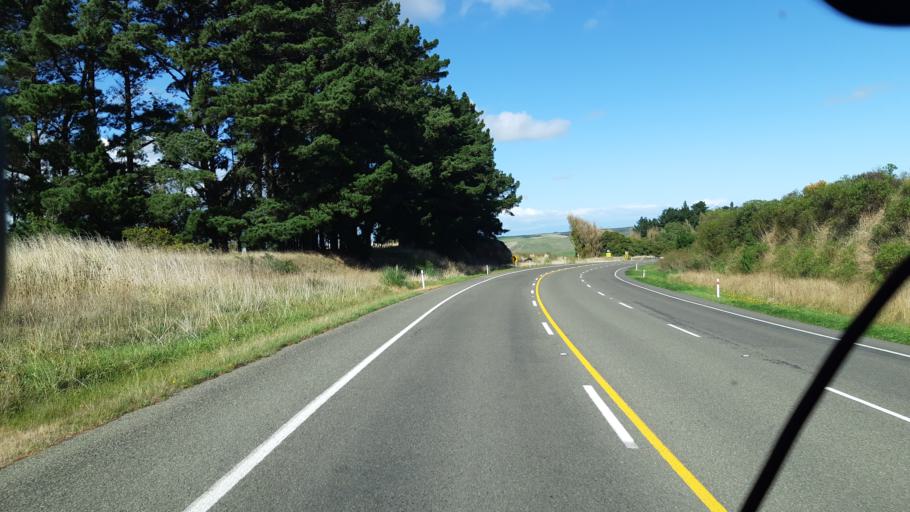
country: NZ
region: Manawatu-Wanganui
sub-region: Wanganui District
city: Wanganui
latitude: -39.9940
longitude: 175.1683
